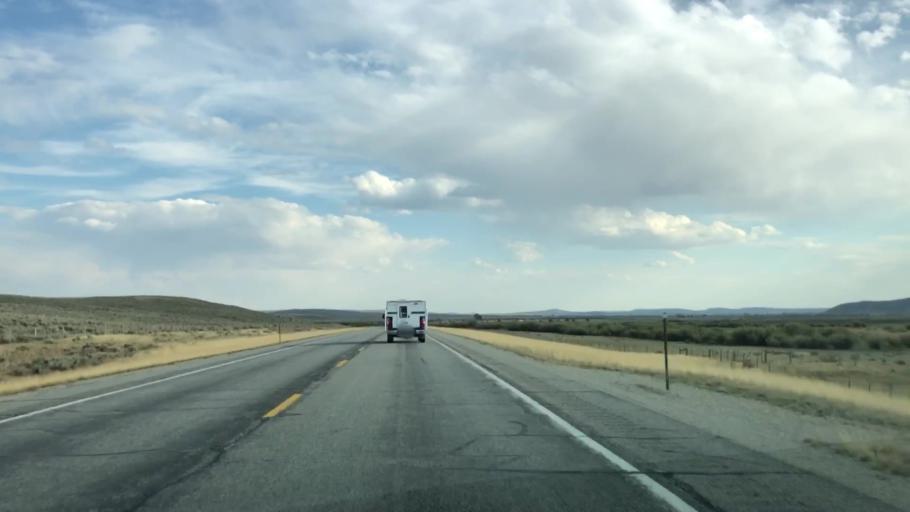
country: US
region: Wyoming
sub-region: Sublette County
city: Pinedale
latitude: 43.0257
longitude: -110.1246
